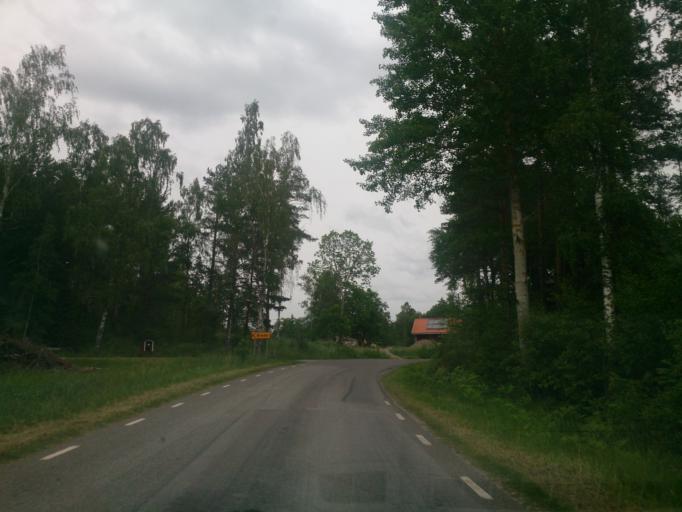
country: SE
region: OEstergoetland
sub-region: Valdemarsviks Kommun
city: Gusum
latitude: 58.3247
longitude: 16.3882
